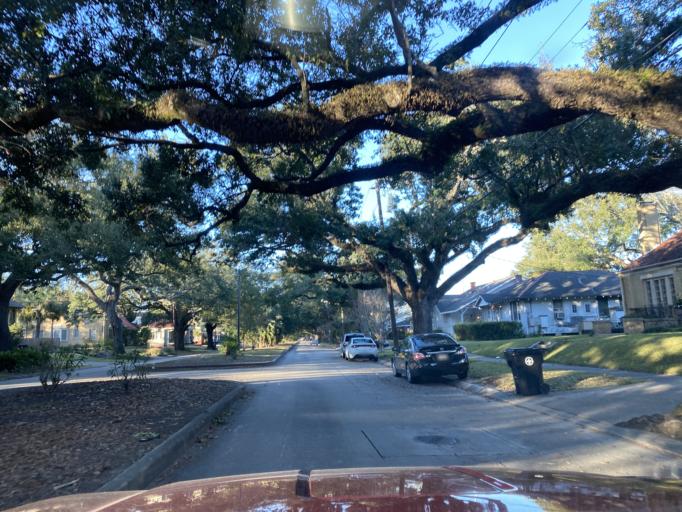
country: US
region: Louisiana
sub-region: Orleans Parish
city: New Orleans
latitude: 30.0036
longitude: -90.0550
